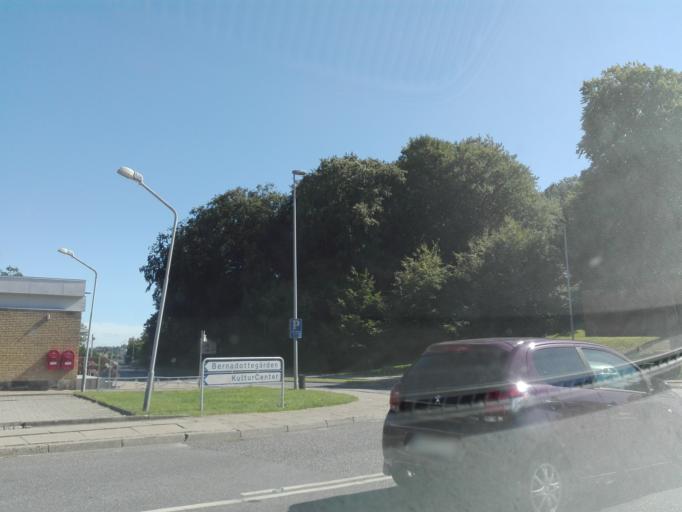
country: DK
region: North Denmark
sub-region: Mariagerfjord Kommune
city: Hadsund
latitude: 56.7177
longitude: 10.1110
